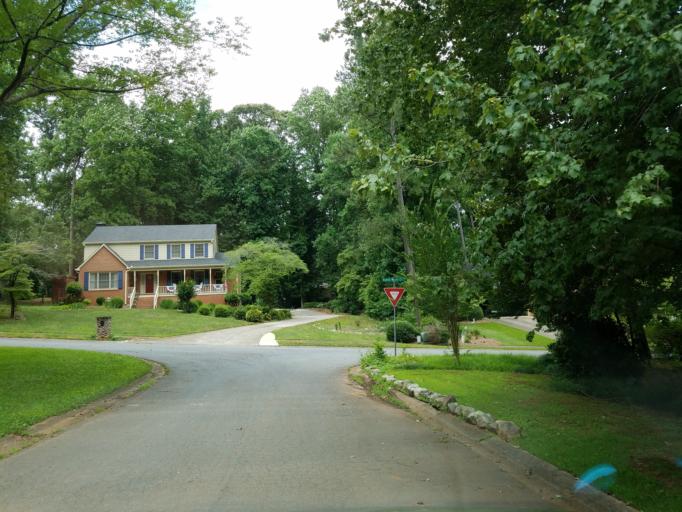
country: US
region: Georgia
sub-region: Cobb County
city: Marietta
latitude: 33.9491
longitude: -84.4858
